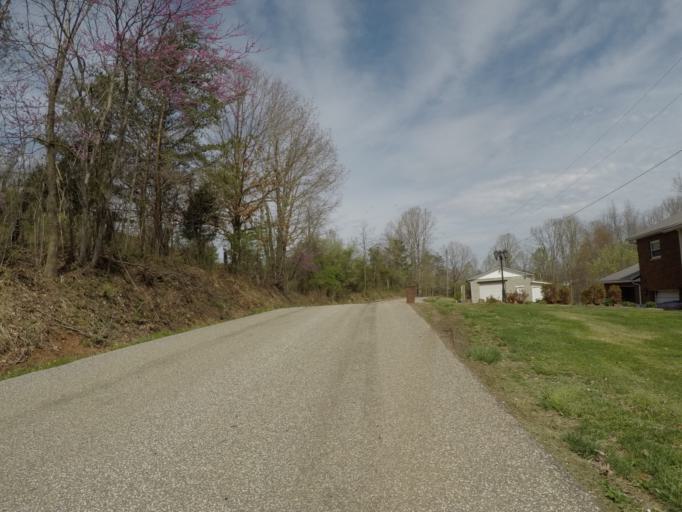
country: US
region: West Virginia
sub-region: Wayne County
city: Lavalette
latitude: 38.3319
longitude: -82.3638
